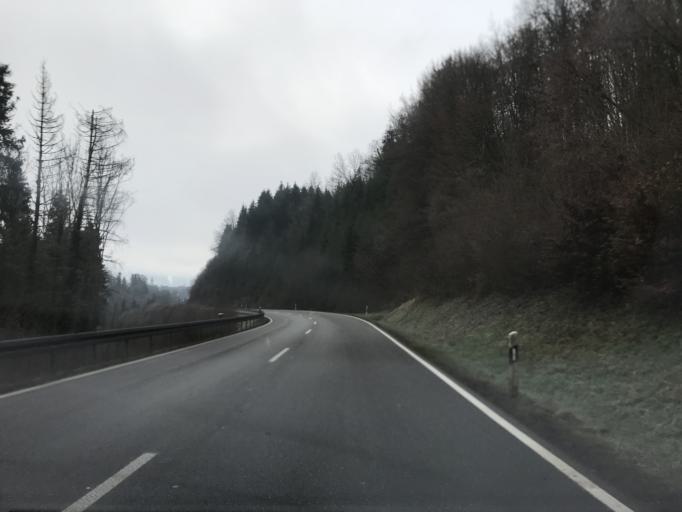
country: DE
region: Baden-Wuerttemberg
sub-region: Freiburg Region
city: Hasel
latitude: 47.6421
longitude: 7.8933
